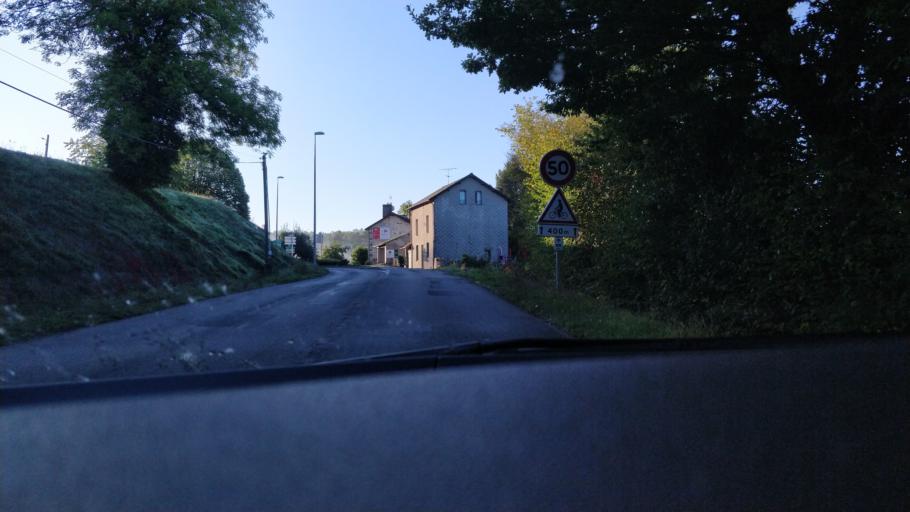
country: FR
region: Limousin
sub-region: Departement de la Creuse
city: Bourganeuf
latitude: 45.9532
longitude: 1.7451
